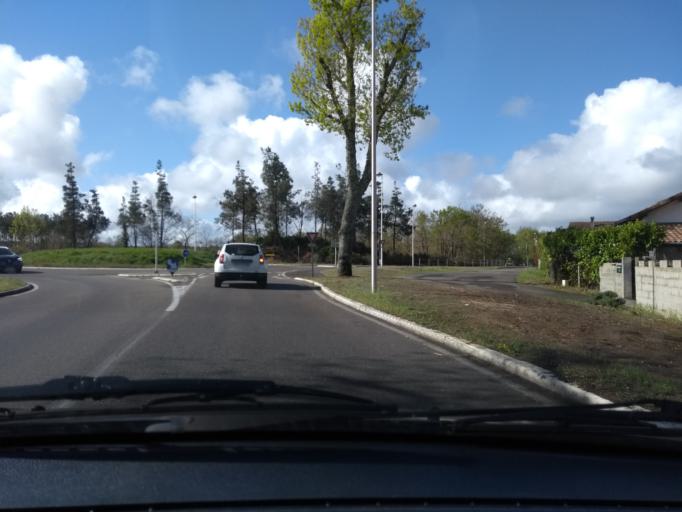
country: FR
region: Aquitaine
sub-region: Departement des Landes
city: Parentis-en-Born
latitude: 44.3408
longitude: -1.0809
